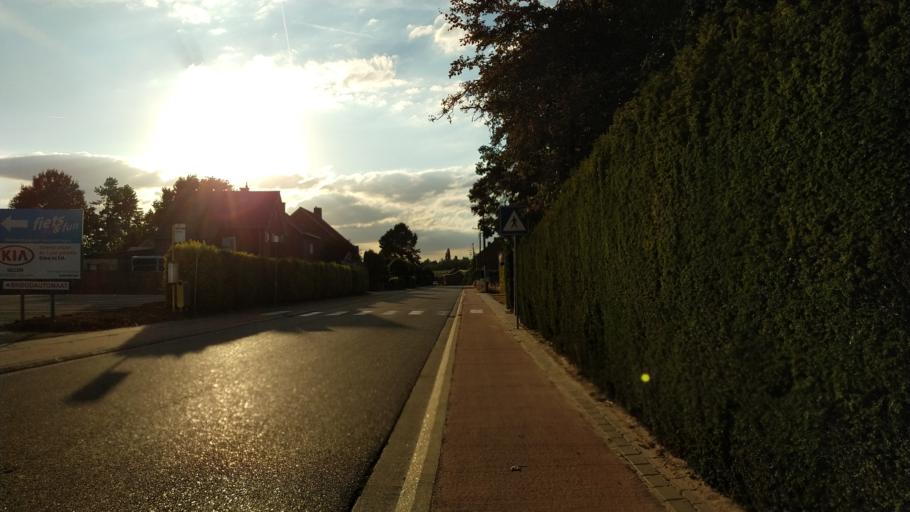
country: BE
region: Flanders
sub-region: Provincie Vlaams-Brabant
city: Bierbeek
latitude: 50.8304
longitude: 4.7520
